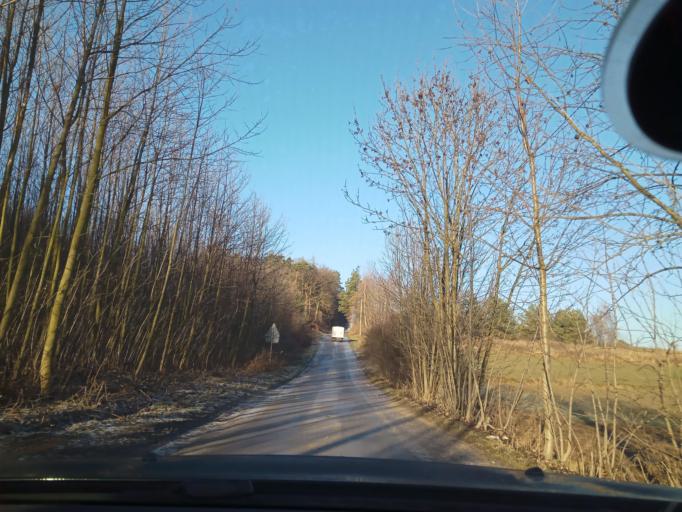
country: PL
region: Lesser Poland Voivodeship
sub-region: Powiat krakowski
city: Michalowice
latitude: 50.1952
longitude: 20.0195
